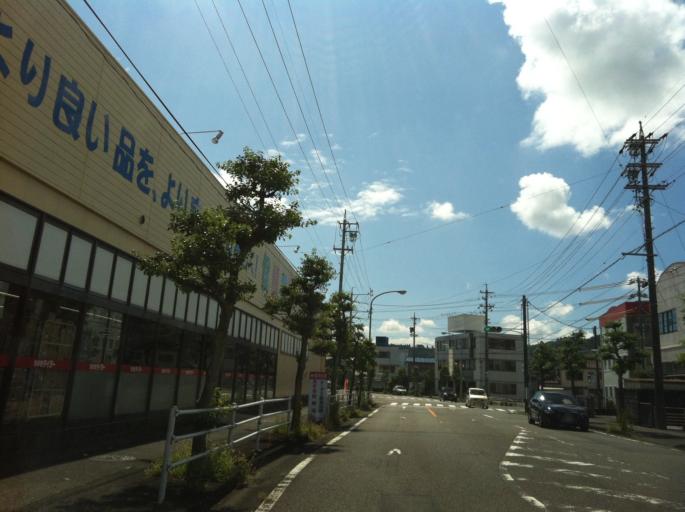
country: JP
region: Shizuoka
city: Kanaya
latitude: 34.8317
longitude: 138.1276
